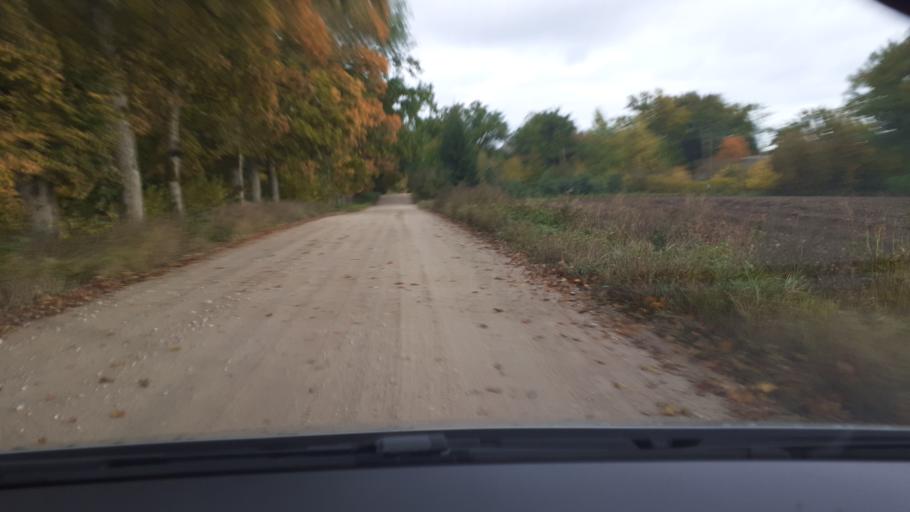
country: LV
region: Kuldigas Rajons
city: Kuldiga
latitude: 57.0232
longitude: 21.9138
